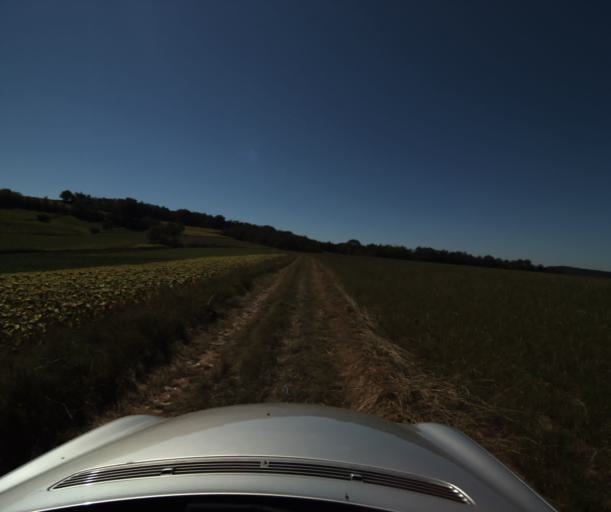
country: FR
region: Midi-Pyrenees
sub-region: Departement de l'Ariege
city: Belesta
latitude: 42.9684
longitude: 1.9278
